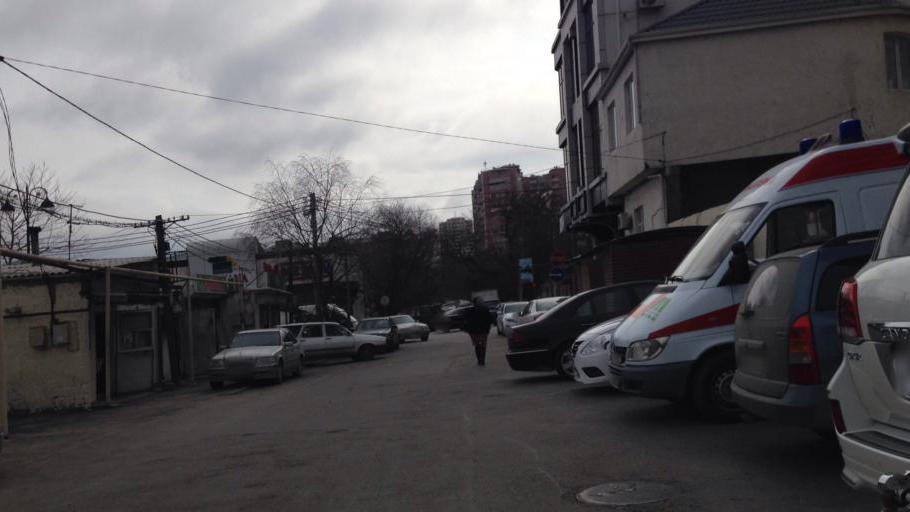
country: AZ
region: Baki
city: Bilajari
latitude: 40.3982
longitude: 49.8285
